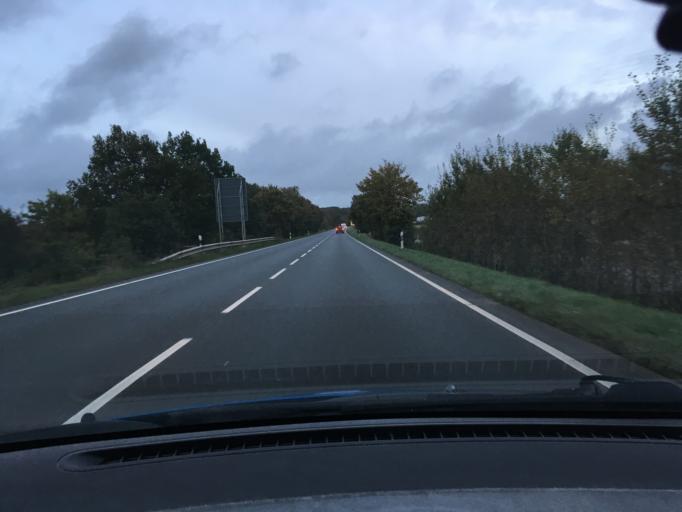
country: DE
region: Schleswig-Holstein
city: Schuby
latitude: 54.5257
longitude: 9.4950
